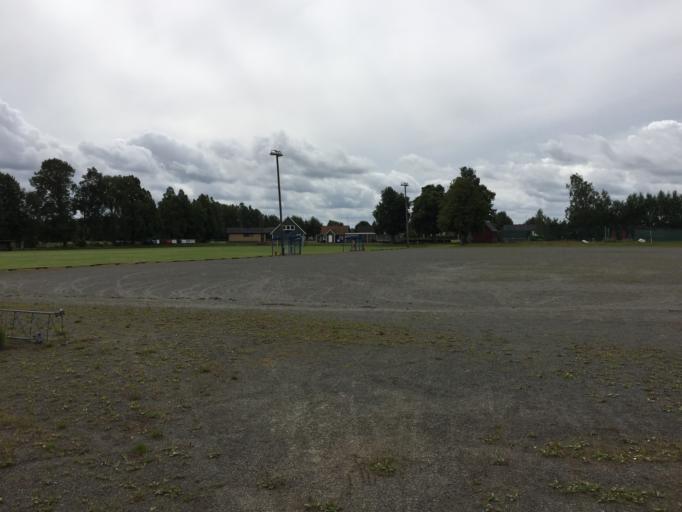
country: SE
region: Skane
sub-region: Hassleholms Kommun
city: Sosdala
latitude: 56.0451
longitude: 13.6851
